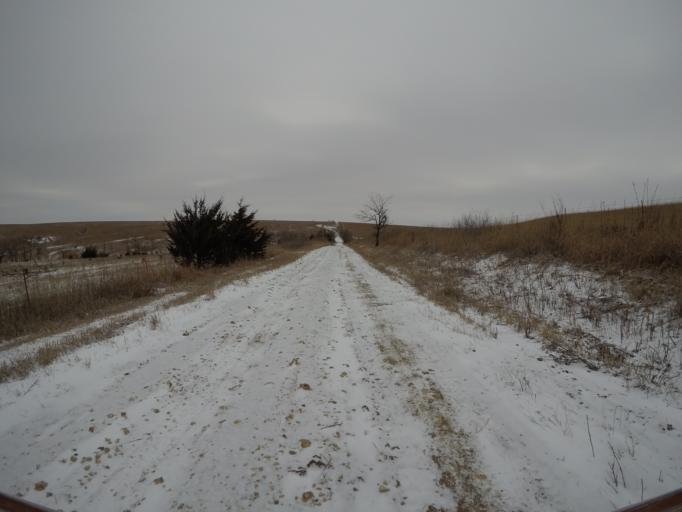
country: US
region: Kansas
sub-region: Wabaunsee County
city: Alma
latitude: 38.8856
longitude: -96.1136
